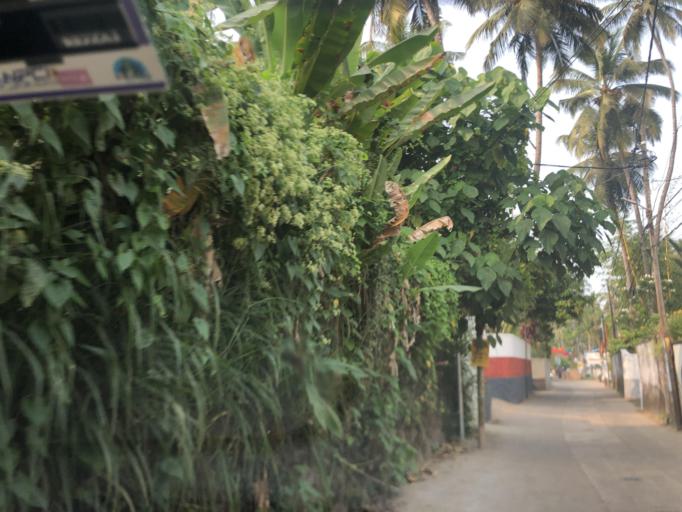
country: IN
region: Kerala
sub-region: Kozhikode
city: Kozhikode
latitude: 11.2792
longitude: 75.7781
